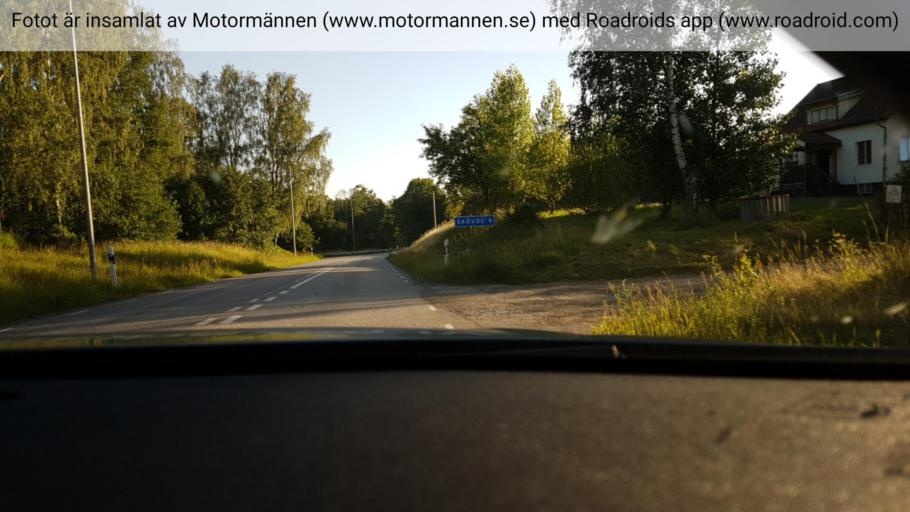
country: SE
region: Vaestra Goetaland
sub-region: Skovde Kommun
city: Stopen
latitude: 58.4351
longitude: 13.9285
